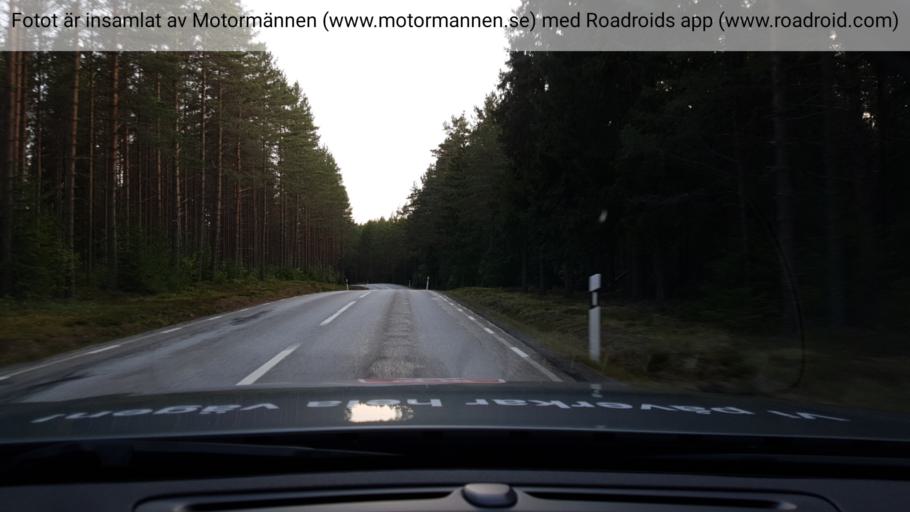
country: SE
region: OErebro
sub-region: Ljusnarsbergs Kommun
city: Kopparberg
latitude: 59.7979
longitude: 14.8209
